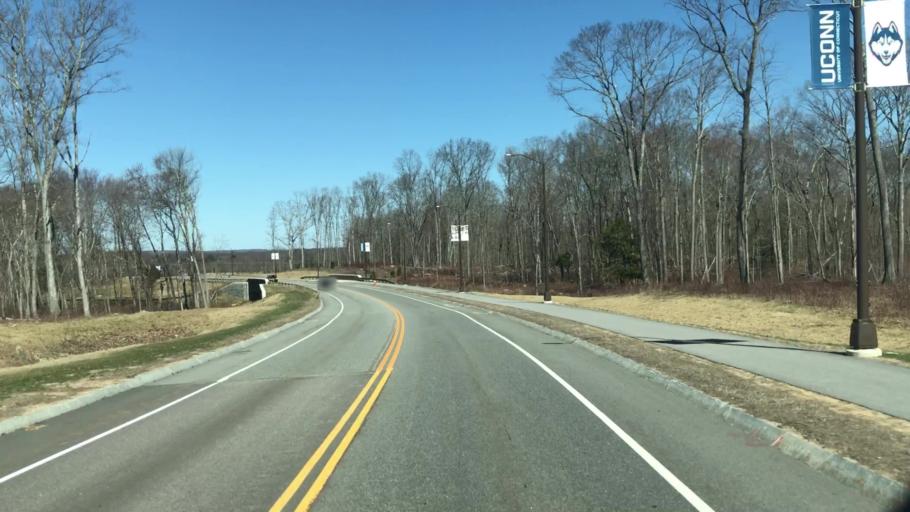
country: US
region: Connecticut
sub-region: Tolland County
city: Storrs
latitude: 41.8223
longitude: -72.2663
